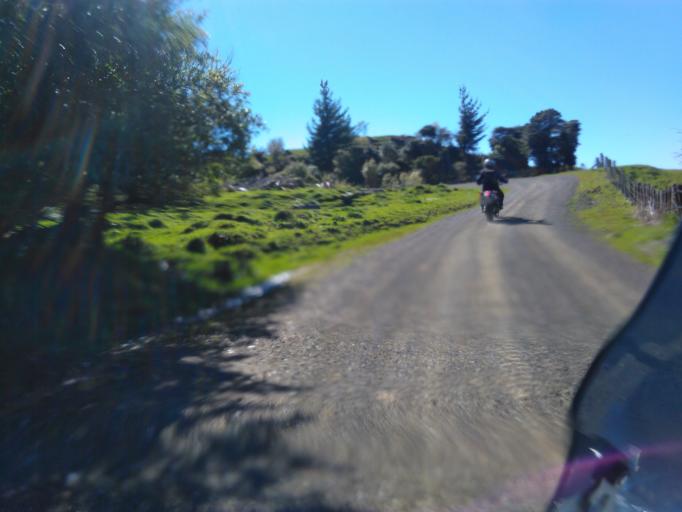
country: NZ
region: Bay of Plenty
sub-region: Opotiki District
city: Opotiki
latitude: -38.3666
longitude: 177.5974
